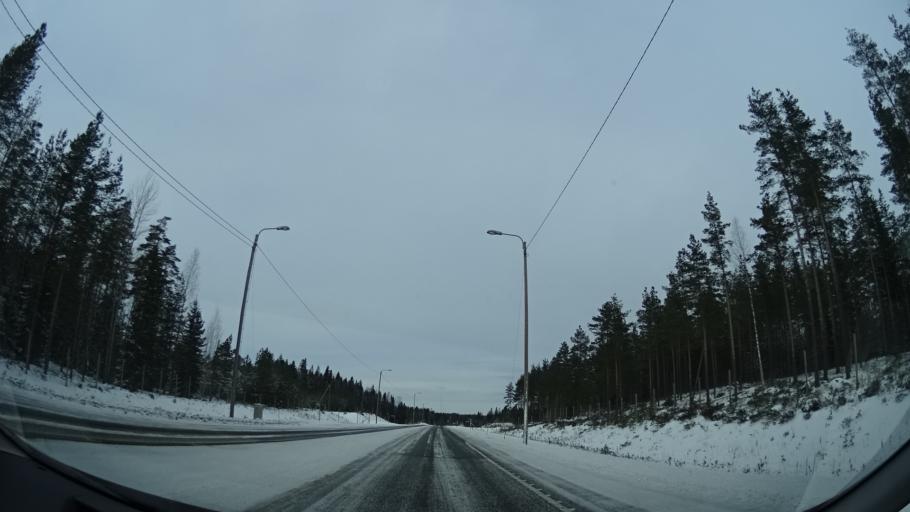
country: FI
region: Uusimaa
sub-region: Helsinki
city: Kaerkoelae
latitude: 60.6360
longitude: 23.9016
